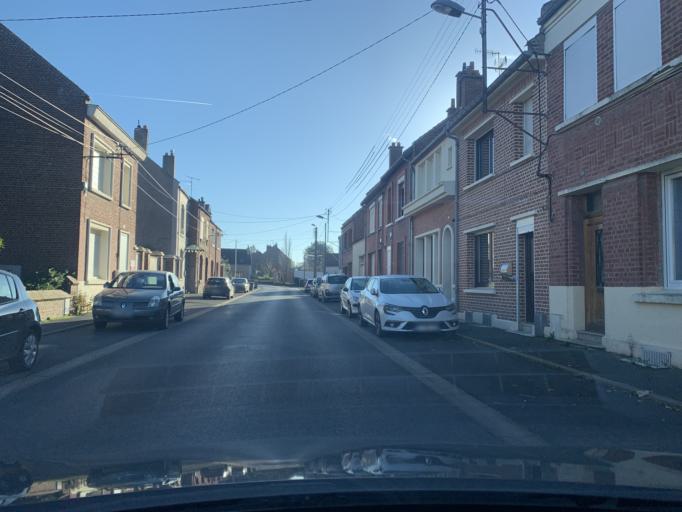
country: FR
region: Nord-Pas-de-Calais
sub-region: Departement du Nord
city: Cambrai
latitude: 50.1688
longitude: 3.2548
